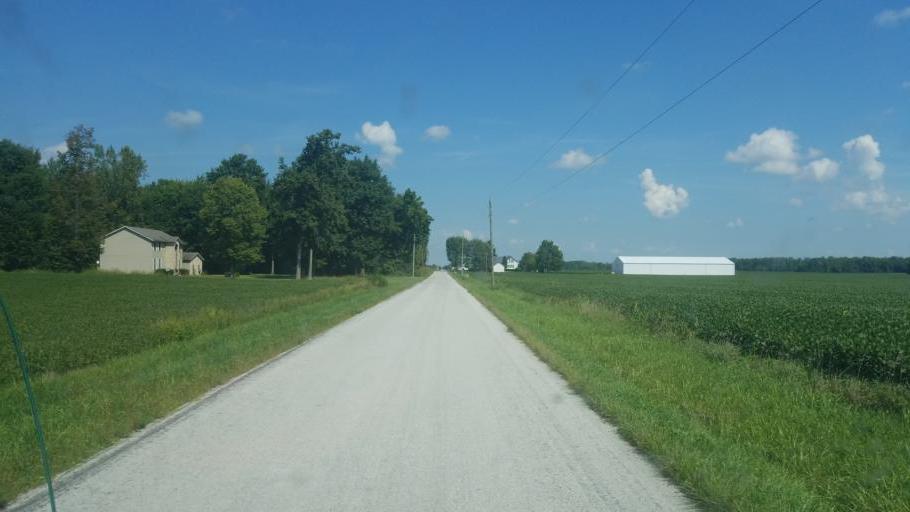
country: US
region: Ohio
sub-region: Hardin County
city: Kenton
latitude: 40.6670
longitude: -83.4957
